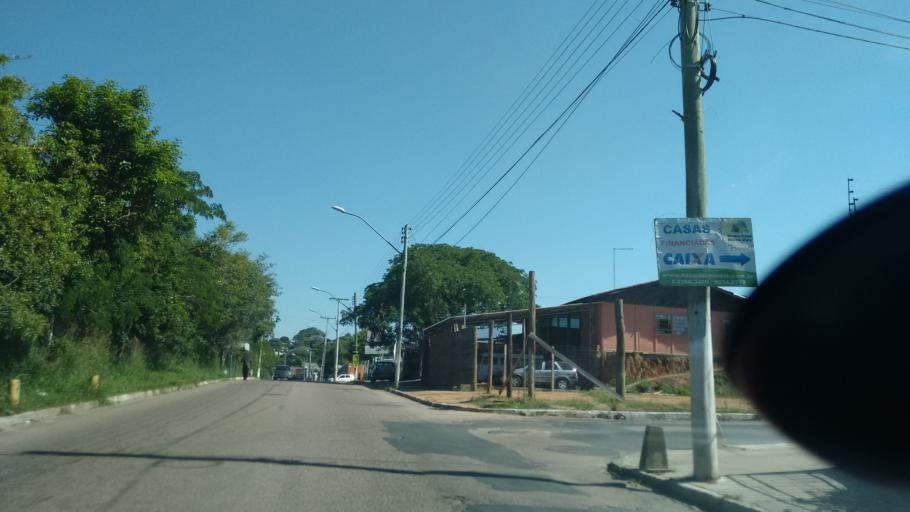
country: BR
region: Rio Grande do Sul
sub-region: Viamao
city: Viamao
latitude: -30.0494
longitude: -51.0985
